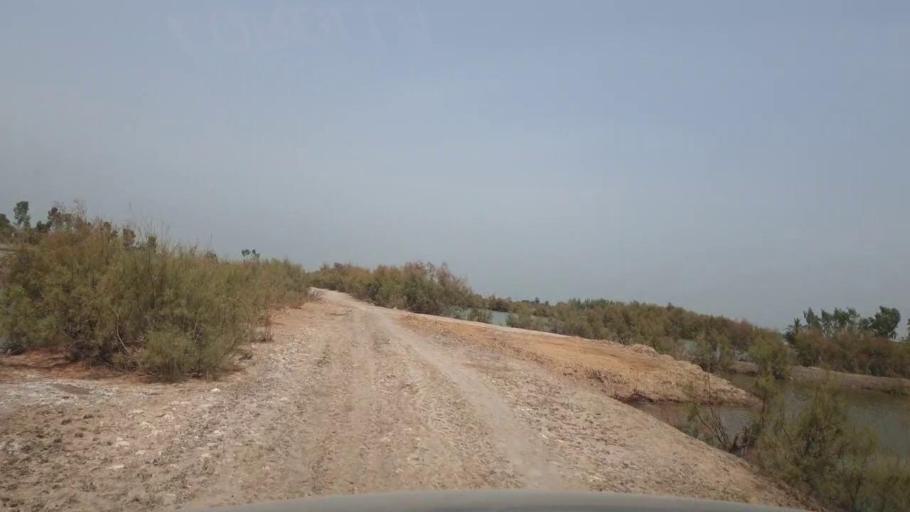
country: PK
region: Sindh
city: Garhi Yasin
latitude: 27.9204
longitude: 68.4141
